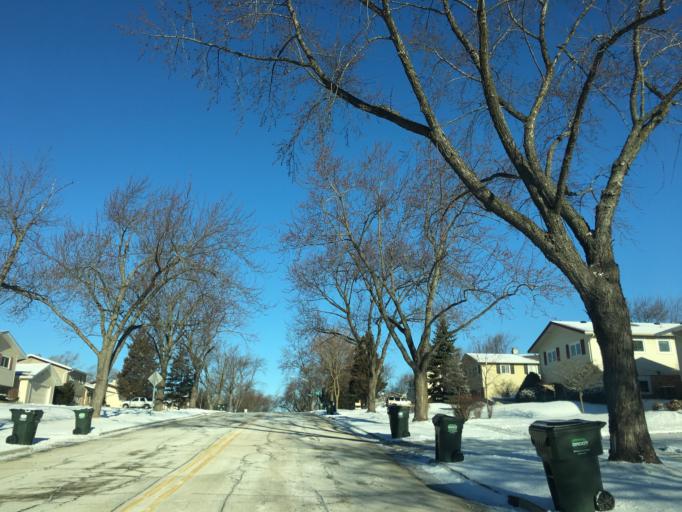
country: US
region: Illinois
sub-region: Cook County
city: Hoffman Estates
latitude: 42.0575
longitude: -88.0918
